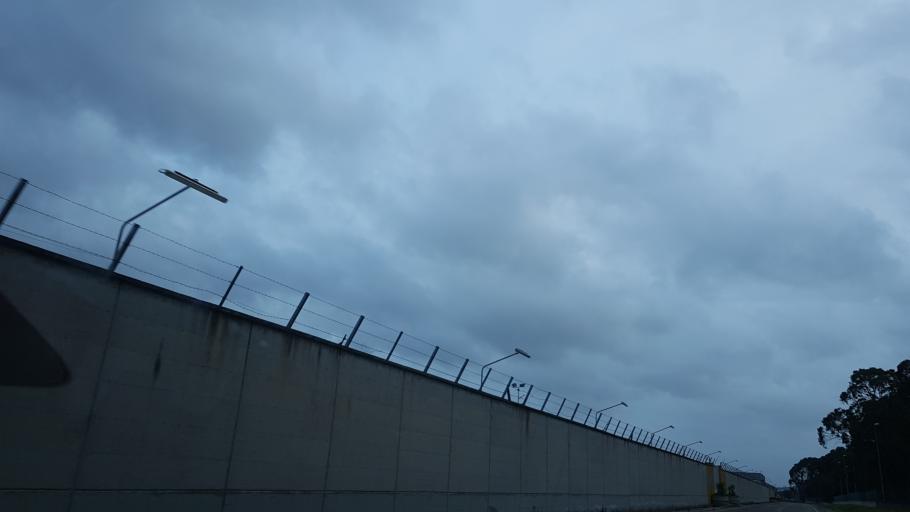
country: IT
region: Apulia
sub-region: Provincia di Brindisi
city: Brindisi
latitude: 40.6331
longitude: 17.9141
